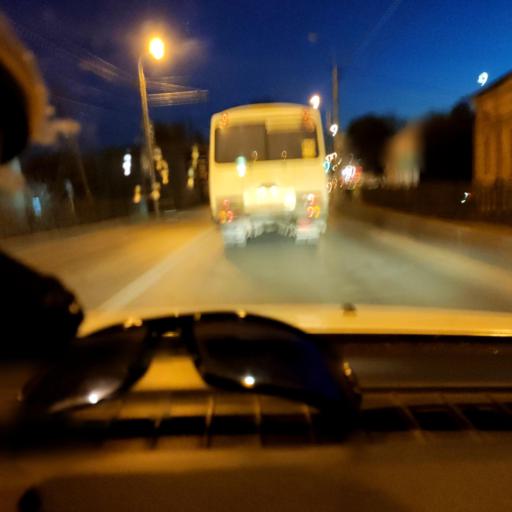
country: RU
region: Samara
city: Rozhdestveno
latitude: 53.1697
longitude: 50.0757
